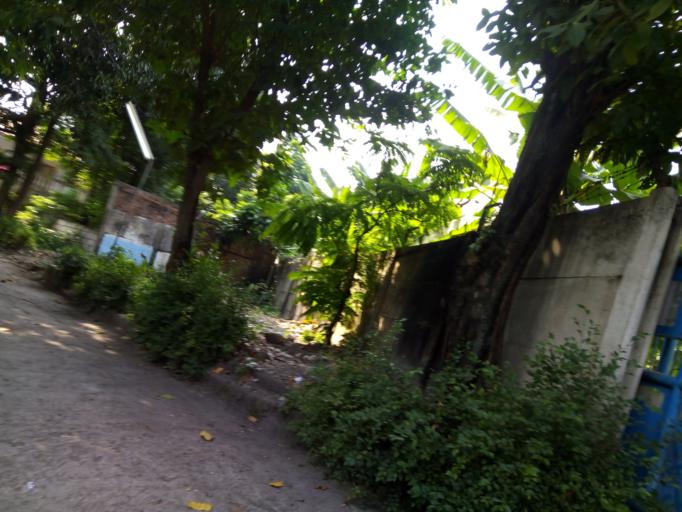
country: ID
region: Jakarta Raya
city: Jakarta
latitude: -6.2058
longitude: 106.8302
